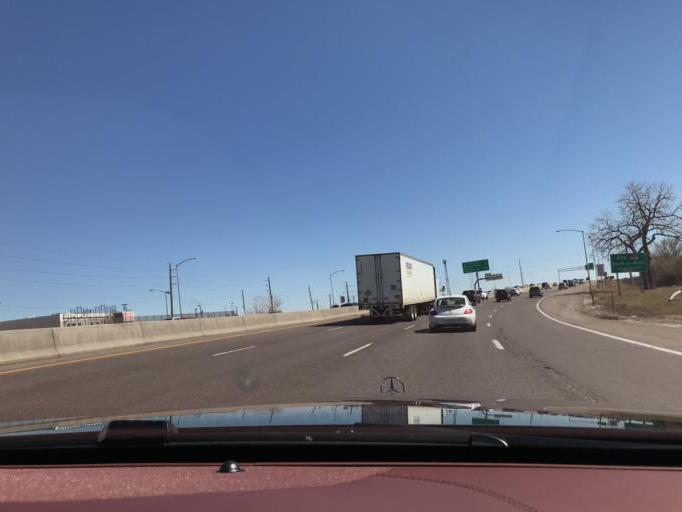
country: US
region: Colorado
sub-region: Adams County
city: Berkley
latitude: 39.7835
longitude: -105.0031
